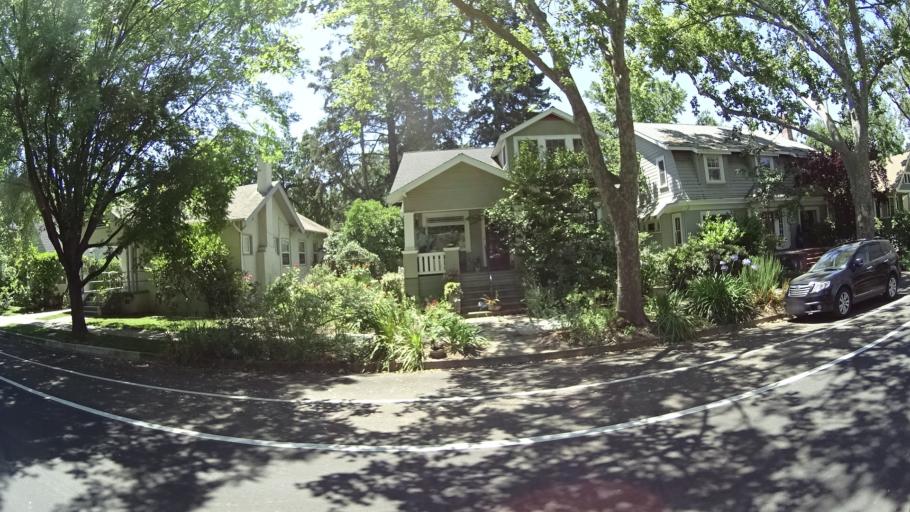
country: US
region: California
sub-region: Sacramento County
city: Sacramento
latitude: 38.5490
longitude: -121.4807
